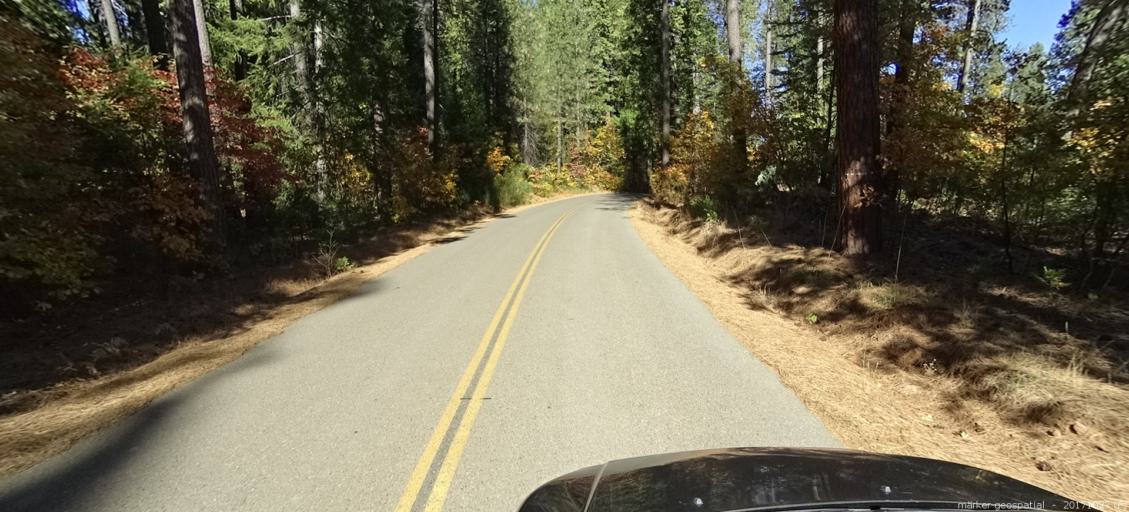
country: US
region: California
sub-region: Shasta County
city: Shingletown
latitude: 40.7327
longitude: -121.9233
